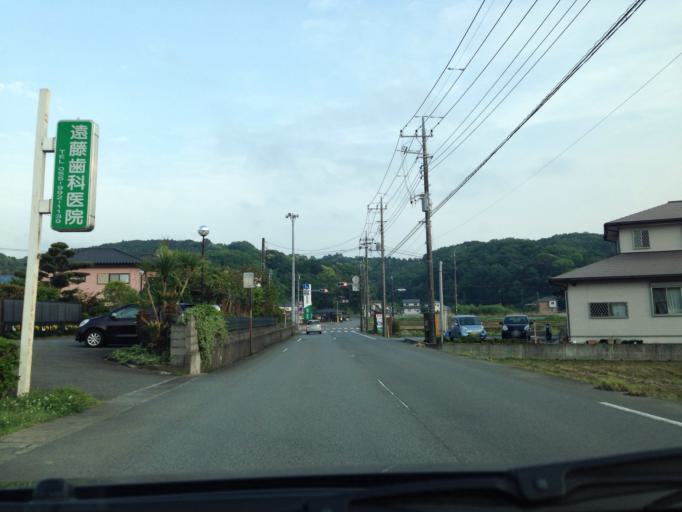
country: JP
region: Shizuoka
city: Mishima
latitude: 35.1688
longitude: 138.9220
